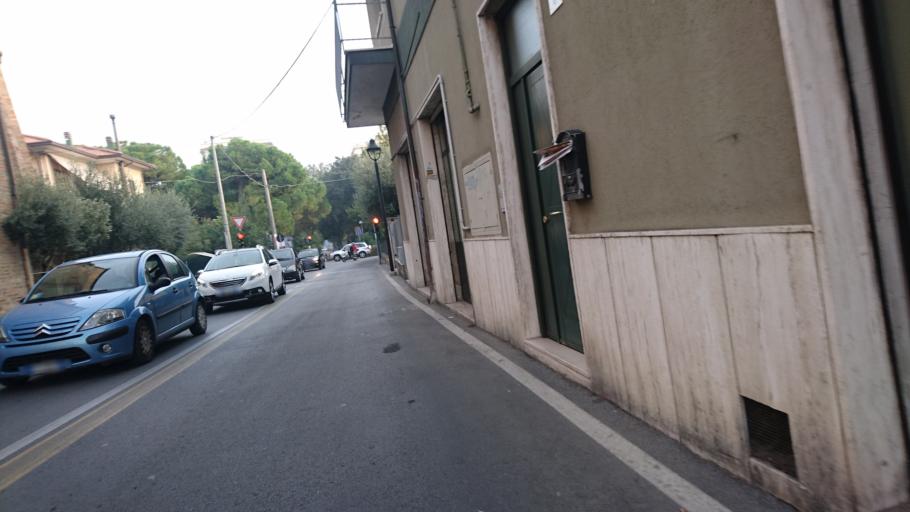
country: IT
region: Emilia-Romagna
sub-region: Provincia di Rimini
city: Rimini
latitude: 44.0585
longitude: 12.5733
